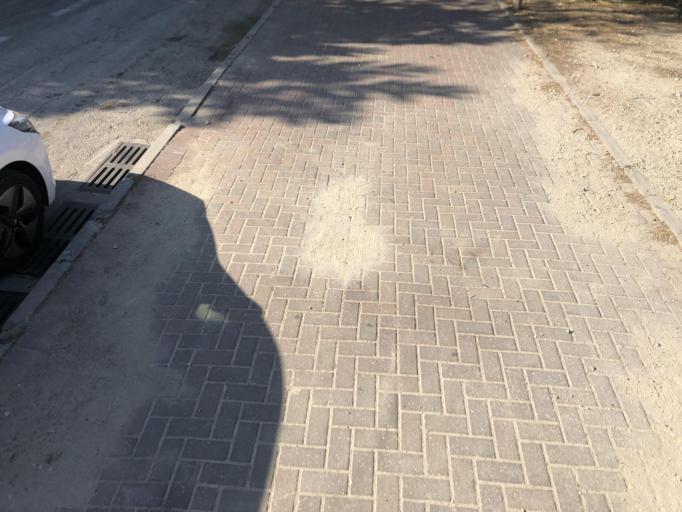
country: IL
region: Central District
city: Yehud
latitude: 32.0362
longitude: 34.8937
